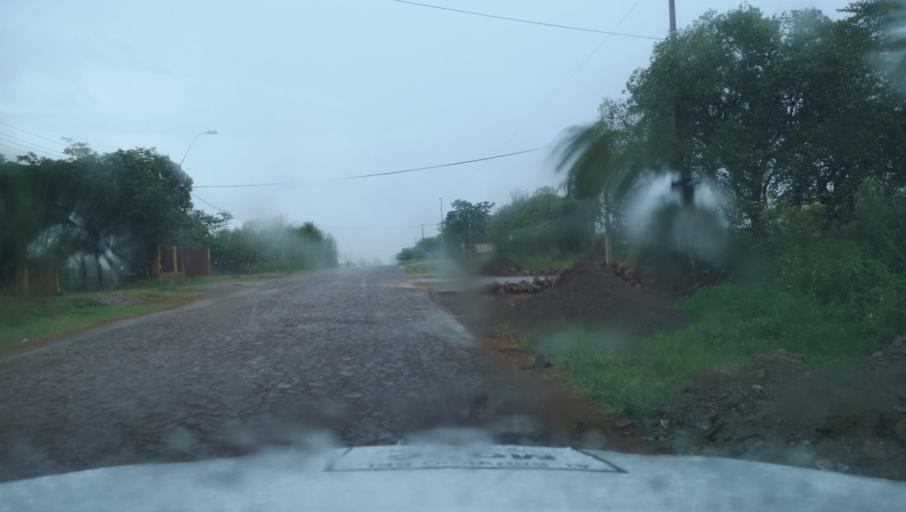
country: PY
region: Misiones
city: Santa Maria
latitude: -26.8951
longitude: -57.0351
